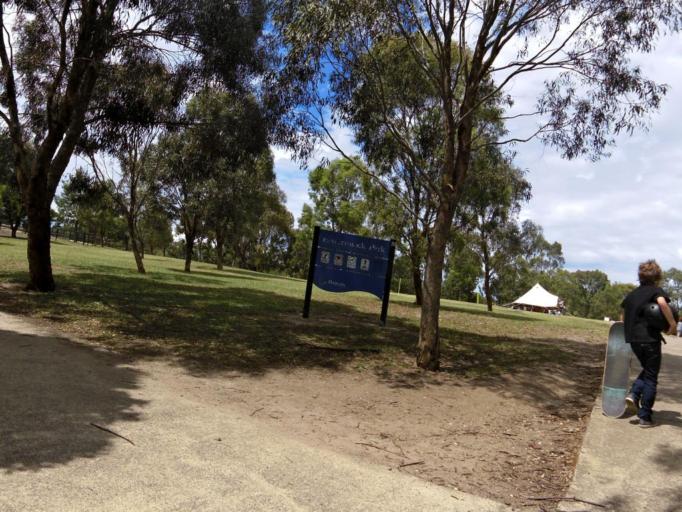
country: AU
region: Victoria
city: Ripponlea
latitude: -37.8880
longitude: 144.9920
